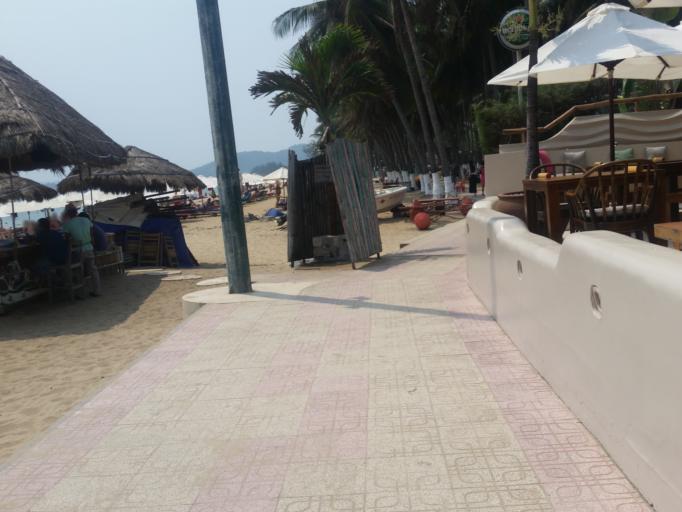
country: VN
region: Khanh Hoa
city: Nha Trang
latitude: 12.2340
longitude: 109.1982
